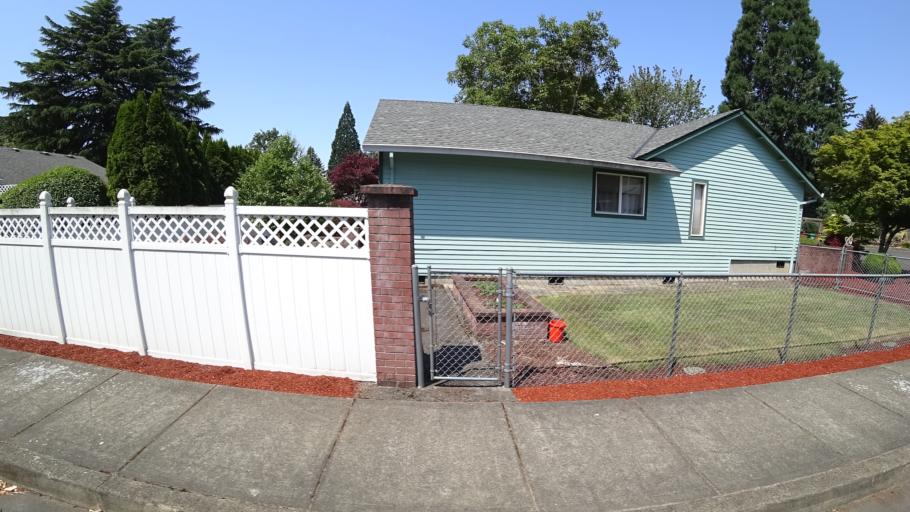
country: US
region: Oregon
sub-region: Clackamas County
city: Oatfield
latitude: 45.4438
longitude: -122.5833
